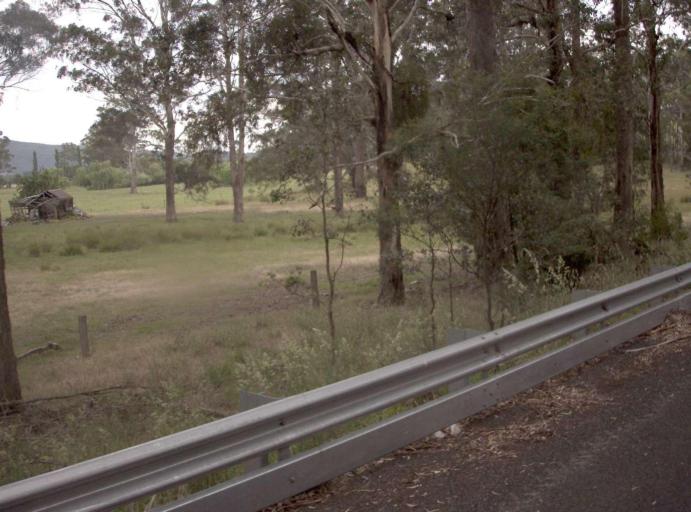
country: AU
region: New South Wales
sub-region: Bombala
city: Bombala
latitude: -37.5069
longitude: 149.1755
